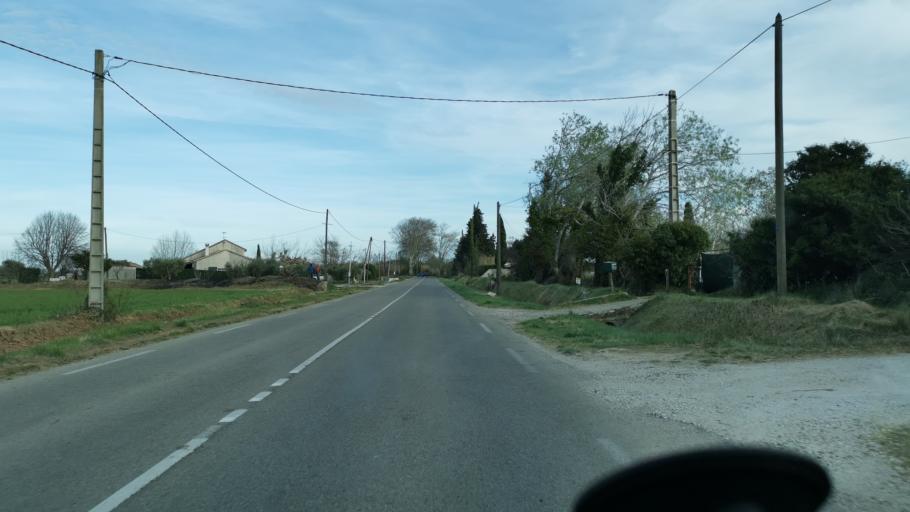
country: FR
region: Provence-Alpes-Cote d'Azur
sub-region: Departement des Bouches-du-Rhone
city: Saint-Martin-de-Crau
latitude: 43.6424
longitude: 4.7325
